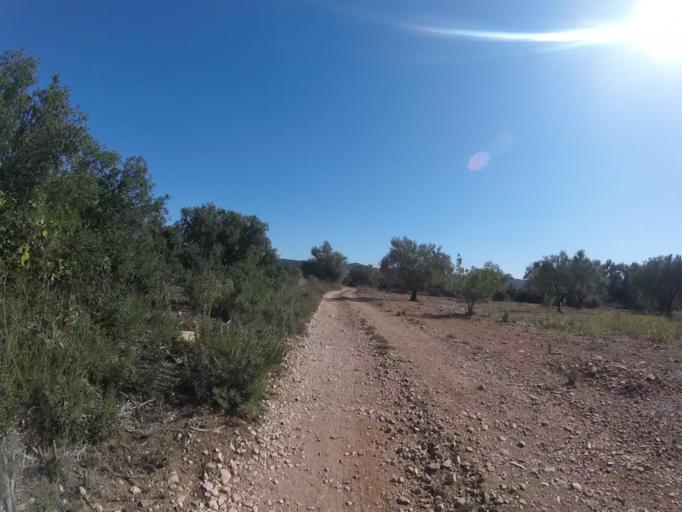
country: ES
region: Valencia
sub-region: Provincia de Castello
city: Cuevas de Vinroma
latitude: 40.2806
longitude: 0.0851
